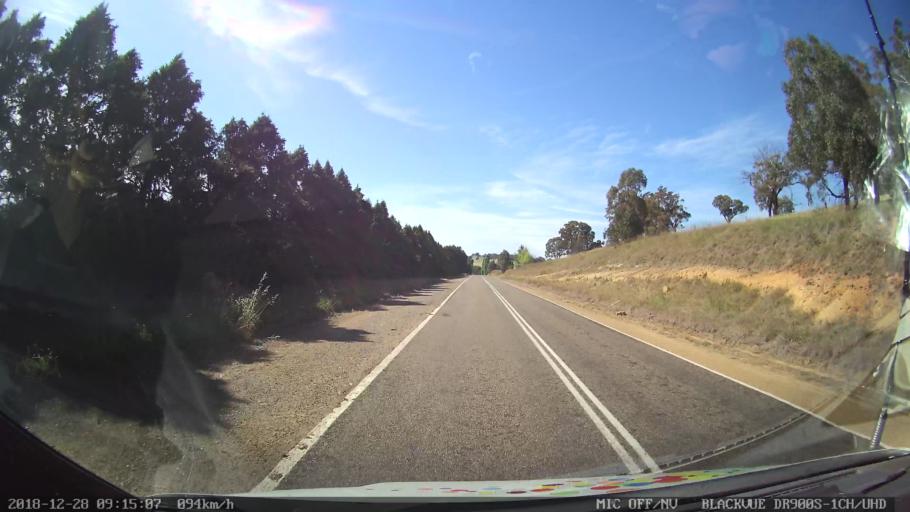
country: AU
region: New South Wales
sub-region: Upper Lachlan Shire
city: Crookwell
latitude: -34.2920
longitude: 149.3475
